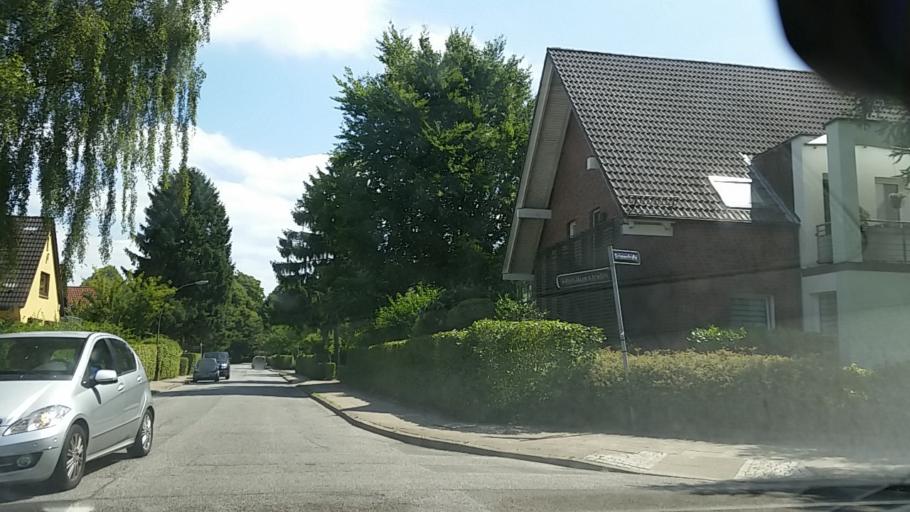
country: DE
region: Schleswig-Holstein
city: Halstenbek
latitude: 53.5805
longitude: 9.8140
